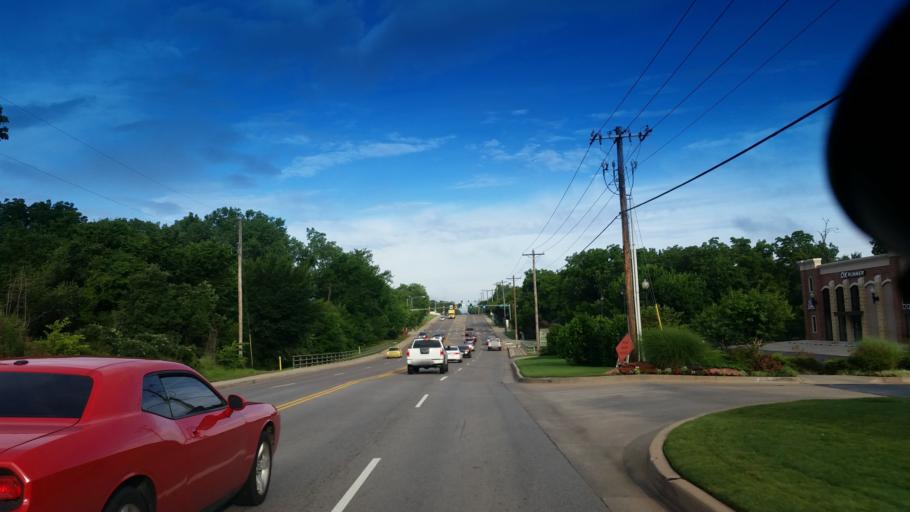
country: US
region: Oklahoma
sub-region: Oklahoma County
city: Edmond
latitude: 35.6383
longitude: -97.4632
